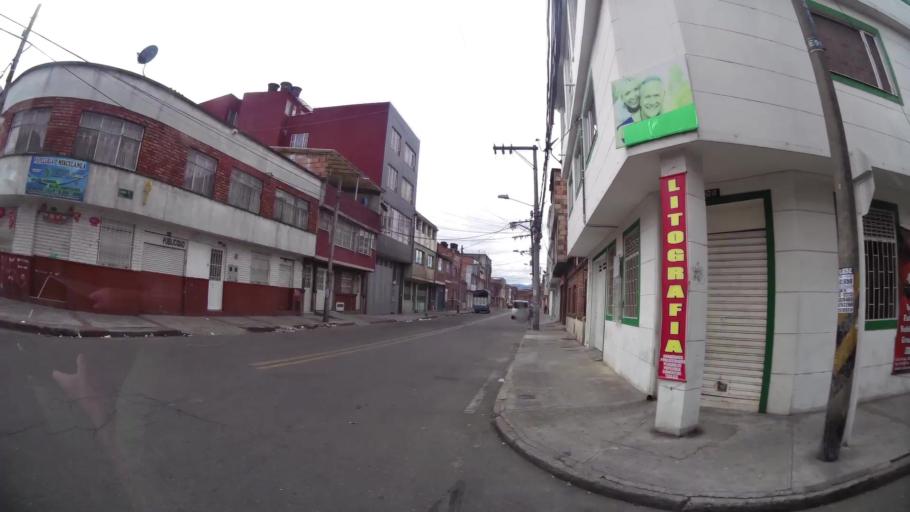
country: CO
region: Bogota D.C.
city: Bogota
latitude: 4.6261
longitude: -74.1181
